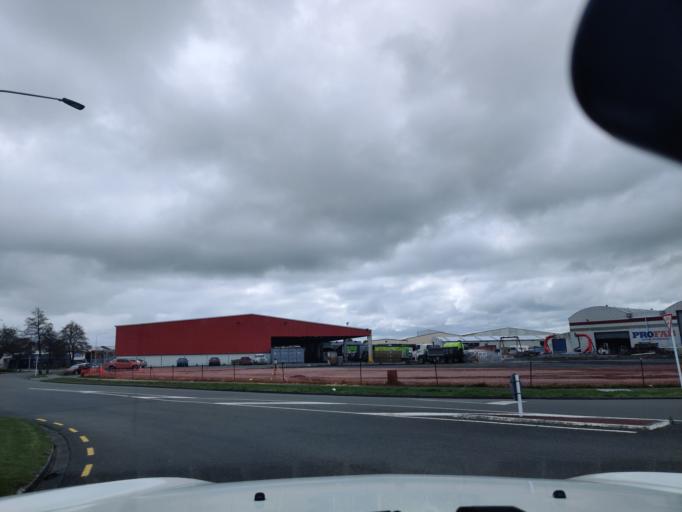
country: NZ
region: Manawatu-Wanganui
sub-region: Palmerston North City
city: Palmerston North
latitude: -40.3362
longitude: 175.6442
